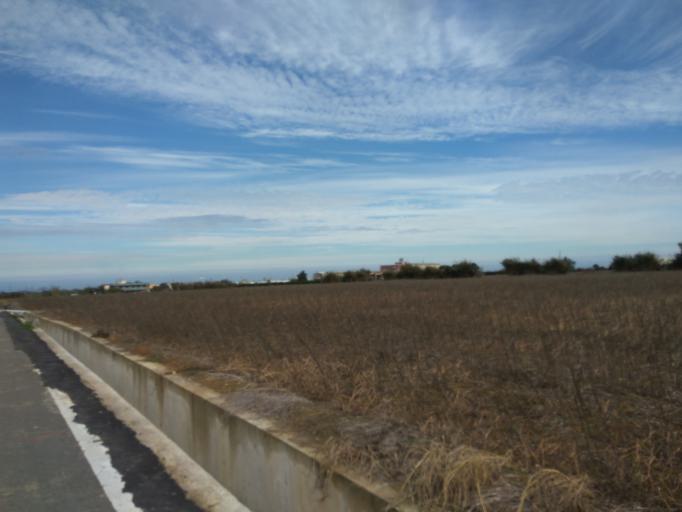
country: TW
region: Taiwan
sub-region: Hsinchu
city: Zhubei
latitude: 25.0085
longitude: 121.0737
